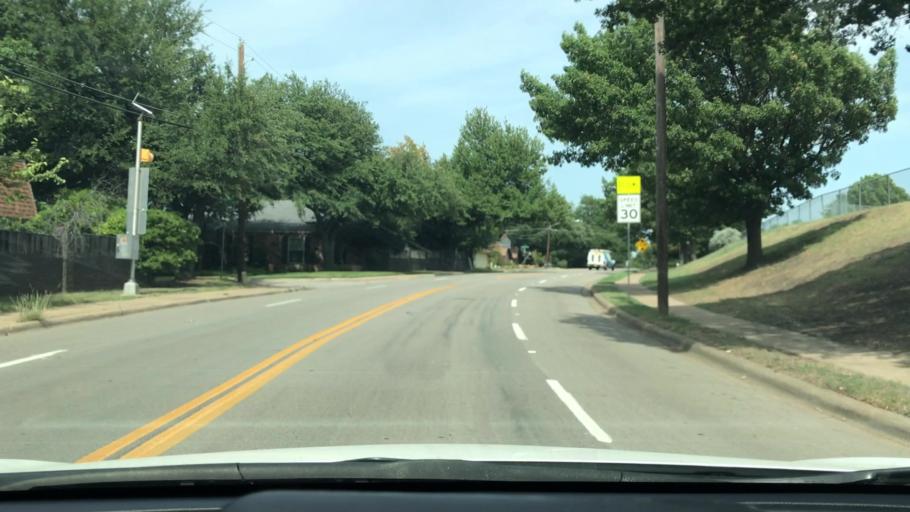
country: US
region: Texas
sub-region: Dallas County
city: University Park
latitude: 32.8871
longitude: -96.7842
